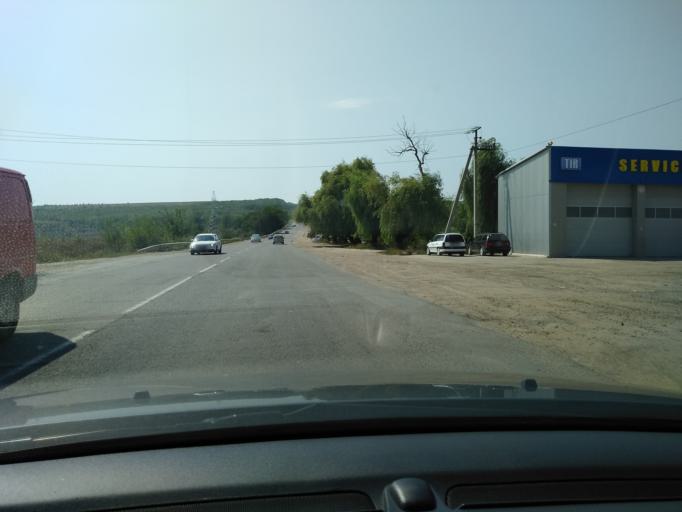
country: MD
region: Chisinau
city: Stauceni
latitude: 47.0863
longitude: 28.8331
